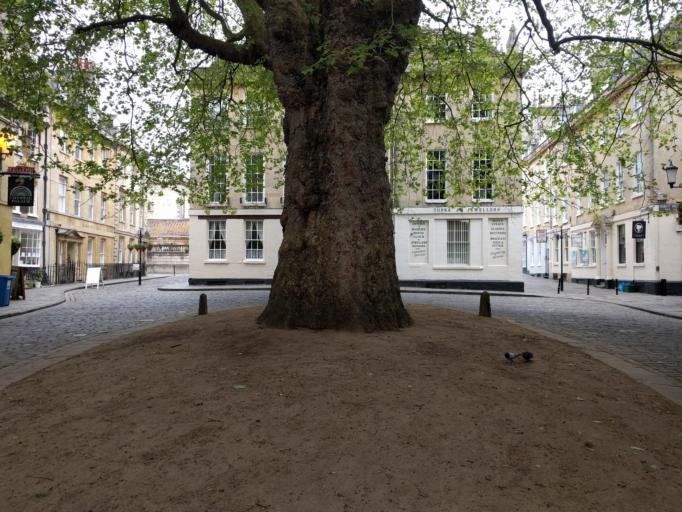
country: GB
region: England
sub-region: Bath and North East Somerset
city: Bath
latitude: 51.3804
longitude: -2.3589
